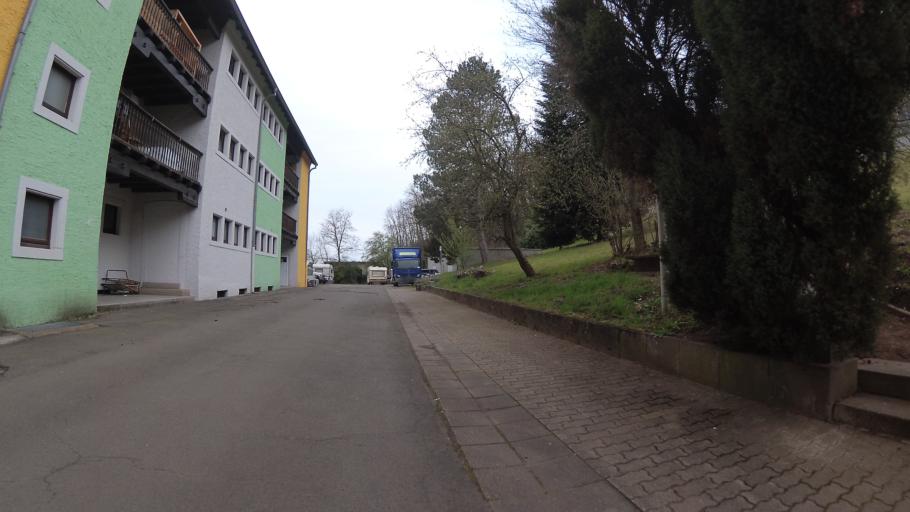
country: DE
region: Saarland
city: Merzig
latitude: 49.4595
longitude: 6.6293
